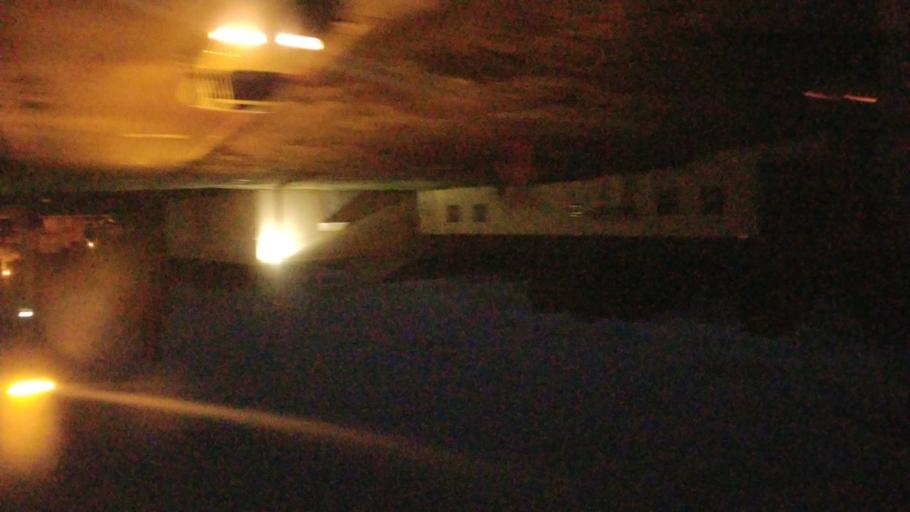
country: US
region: Ohio
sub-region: Columbiana County
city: East Palestine
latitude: 40.8357
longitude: -80.5274
